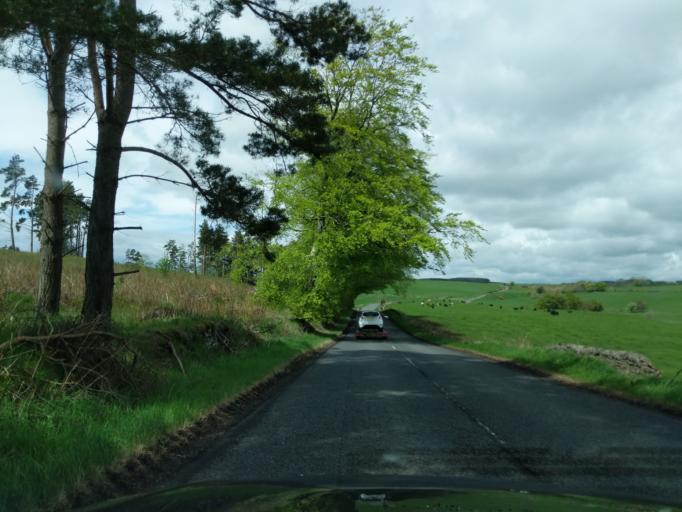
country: GB
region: Scotland
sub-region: The Scottish Borders
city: Earlston
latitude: 55.6971
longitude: -2.5861
